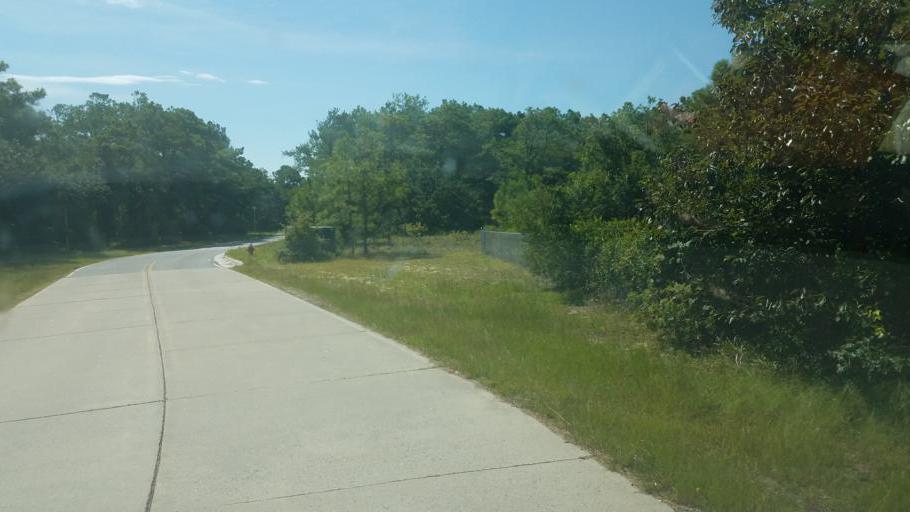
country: US
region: North Carolina
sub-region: Dare County
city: Kill Devil Hills
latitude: 36.0065
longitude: -75.6630
